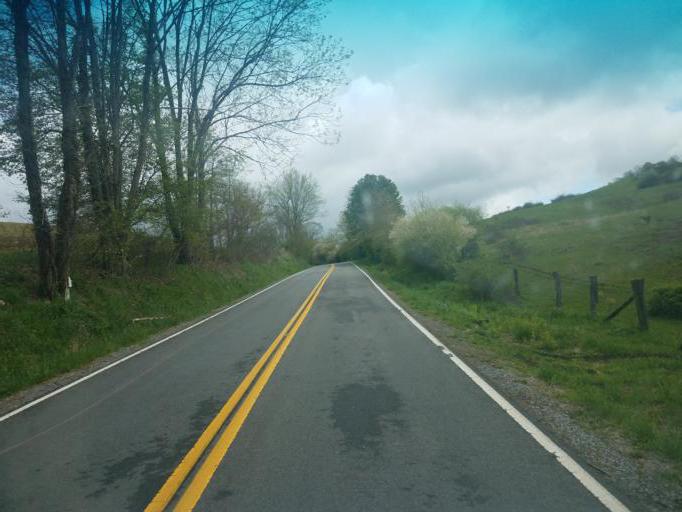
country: US
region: Virginia
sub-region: Smyth County
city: Atkins
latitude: 36.9911
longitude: -81.3845
